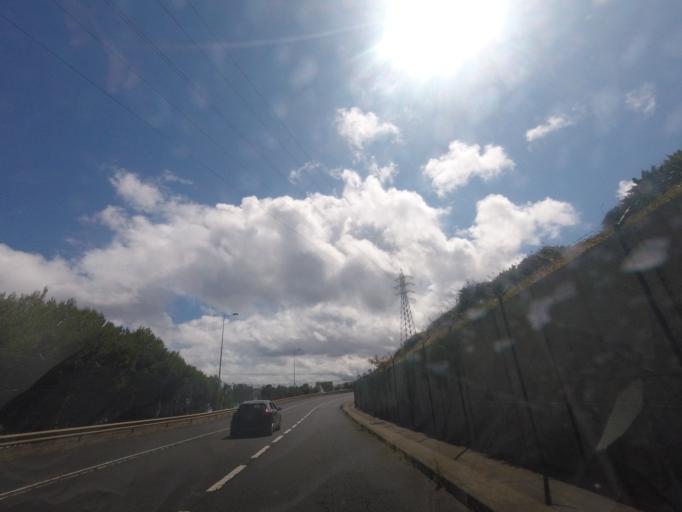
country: PT
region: Madeira
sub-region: Machico
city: Canical
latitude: 32.7421
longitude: -16.7325
